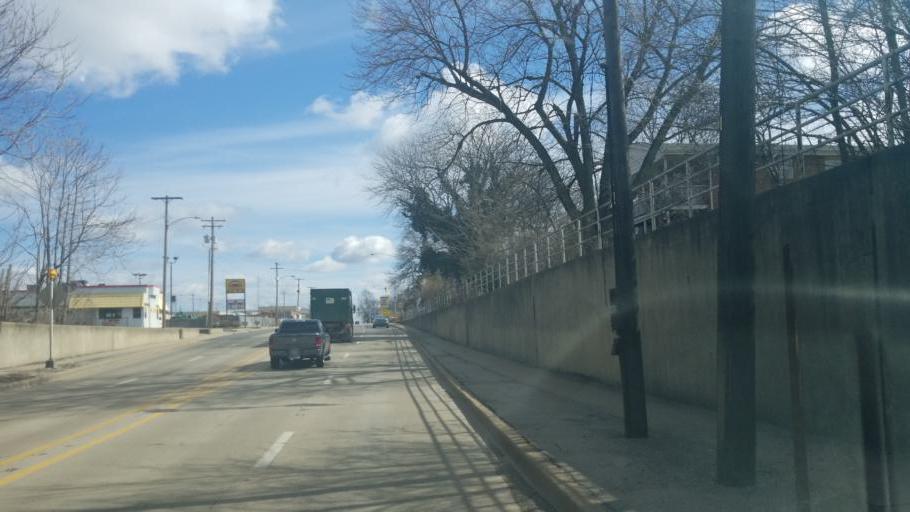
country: US
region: Illinois
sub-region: Macon County
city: Decatur
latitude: 39.8456
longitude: -88.9675
